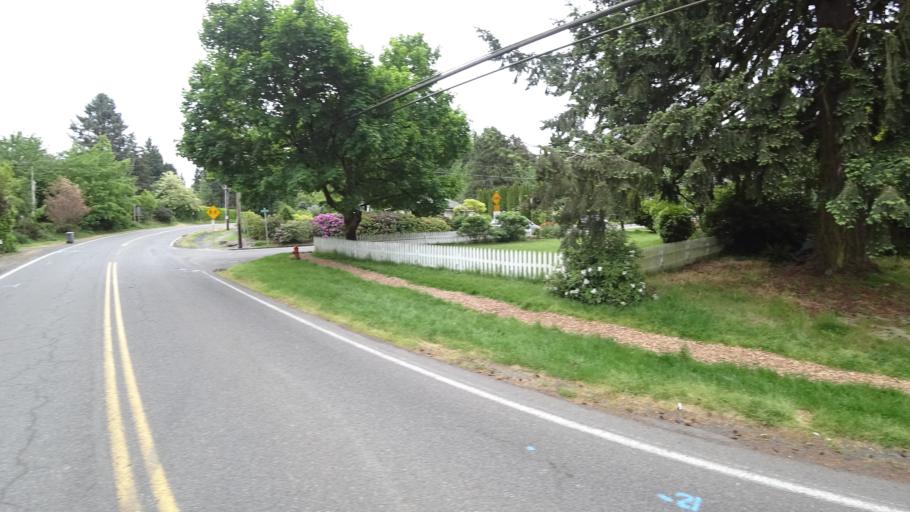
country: US
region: Oregon
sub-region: Washington County
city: Garden Home-Whitford
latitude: 45.4651
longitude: -122.7360
